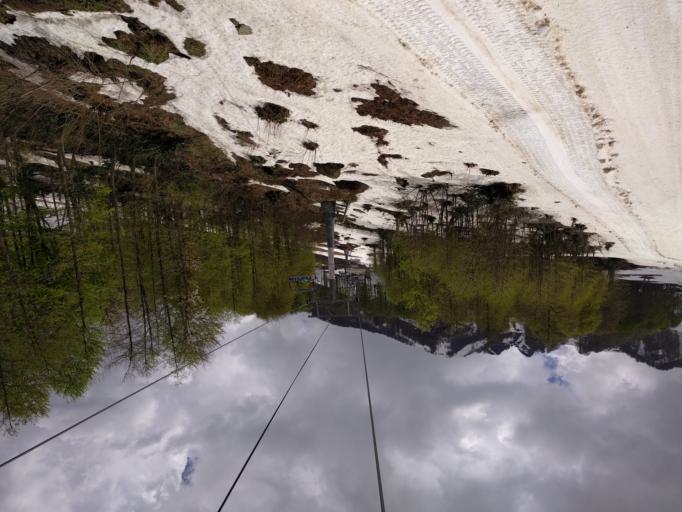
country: RU
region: Krasnodarskiy
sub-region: Sochi City
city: Krasnaya Polyana
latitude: 43.6447
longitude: 40.3218
